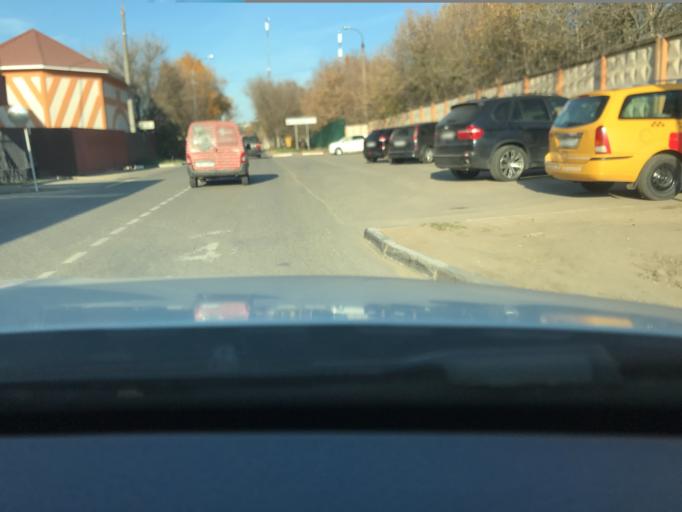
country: RU
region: Moscow
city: Rublevo
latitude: 55.8025
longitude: 37.3733
